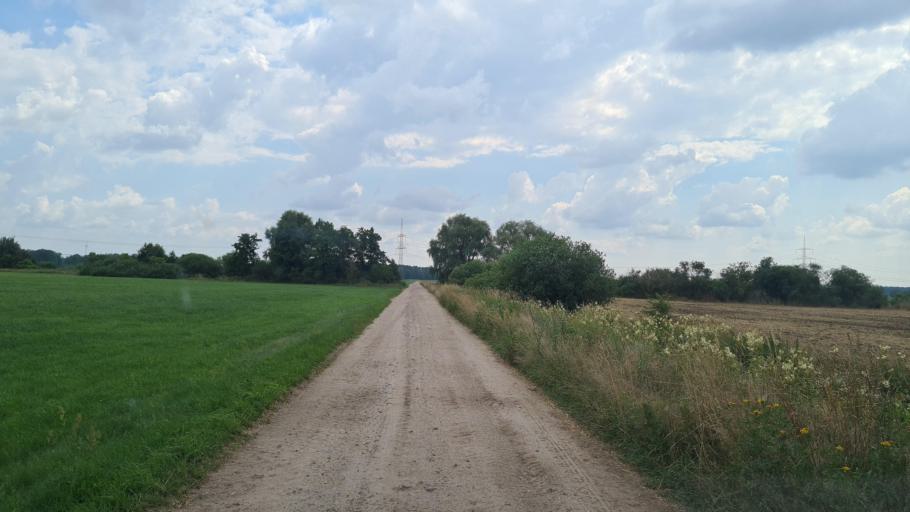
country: DE
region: Brandenburg
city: Sallgast
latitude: 51.6344
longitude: 13.8678
